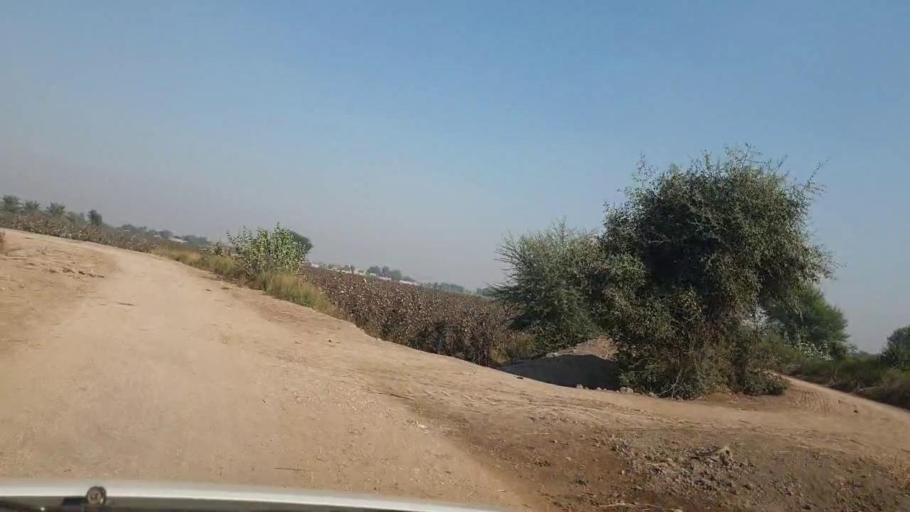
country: PK
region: Sindh
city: Bhan
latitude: 26.6197
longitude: 67.7626
